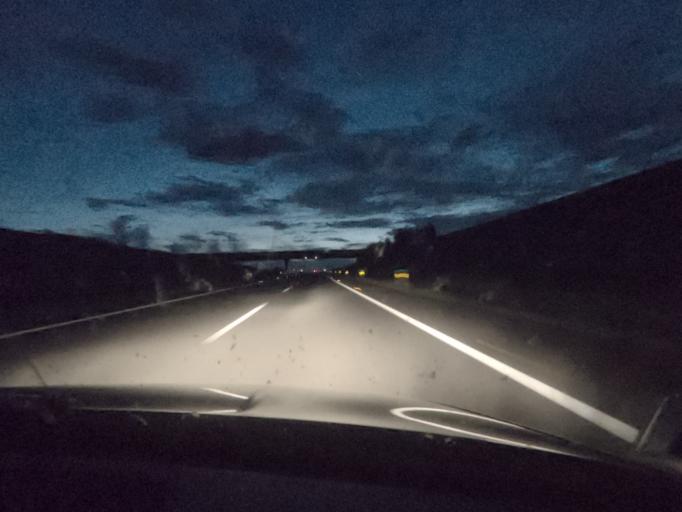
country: ES
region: Extremadura
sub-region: Provincia de Caceres
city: Riolobos
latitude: 39.9737
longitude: -6.3458
